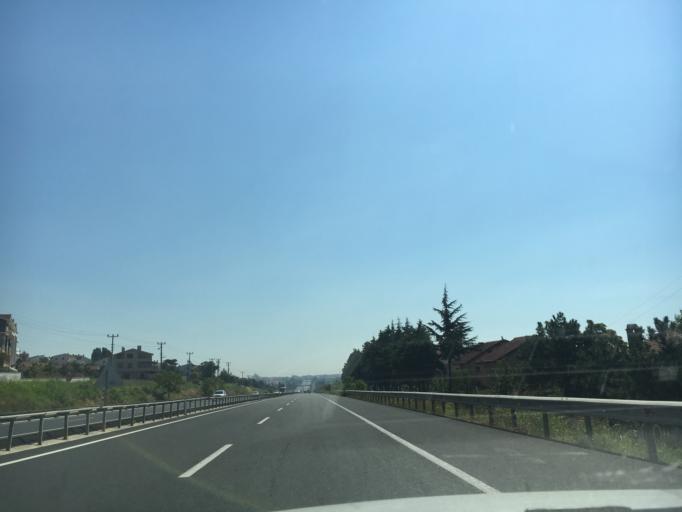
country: TR
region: Tekirdag
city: Marmara Ereglisi
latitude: 40.9702
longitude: 27.9119
